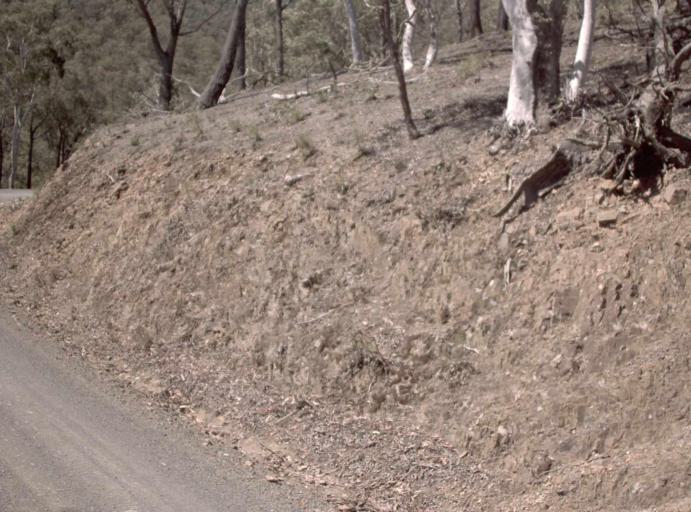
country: AU
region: New South Wales
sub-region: Bombala
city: Bombala
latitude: -37.0979
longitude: 148.6323
